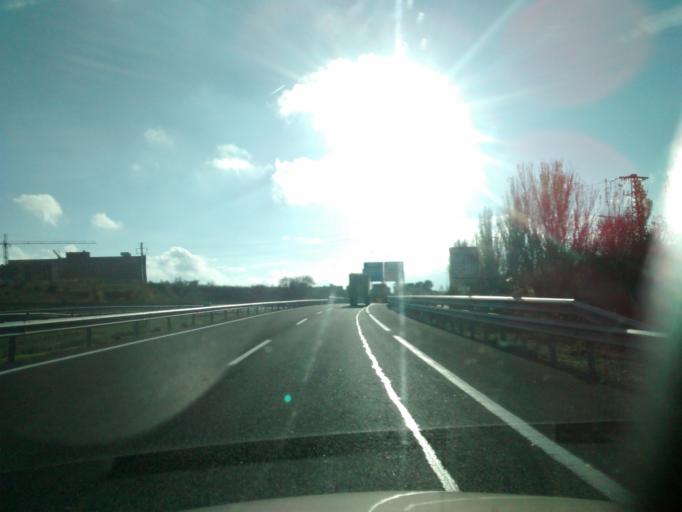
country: ES
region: Castille-La Mancha
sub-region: Provincia de Guadalajara
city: Guadalajara
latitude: 40.6250
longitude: -3.1513
